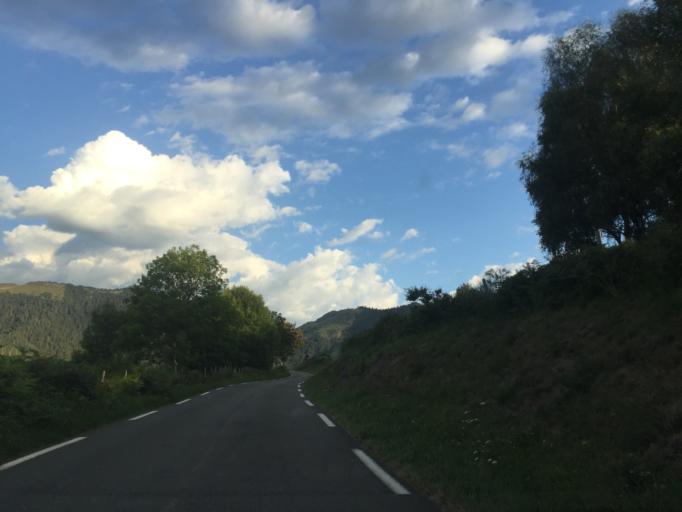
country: FR
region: Midi-Pyrenees
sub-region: Departement des Hautes-Pyrenees
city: Saint-Lary-Soulan
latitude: 42.9254
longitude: 0.3535
